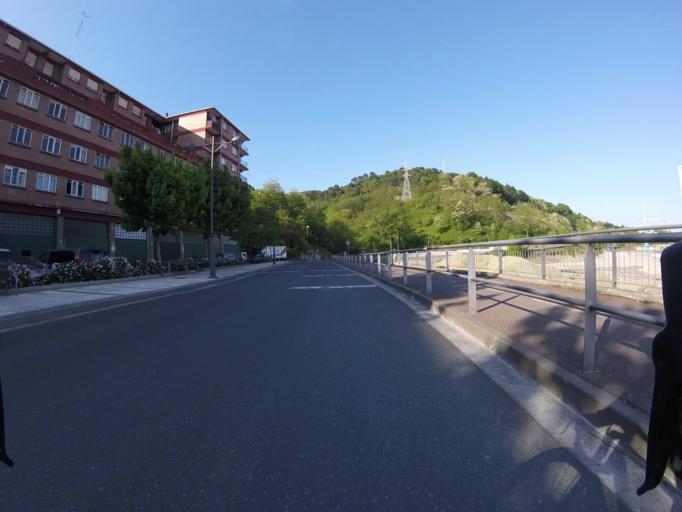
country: ES
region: Basque Country
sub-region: Provincia de Guipuzcoa
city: Lezo
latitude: 43.3235
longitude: -1.9113
